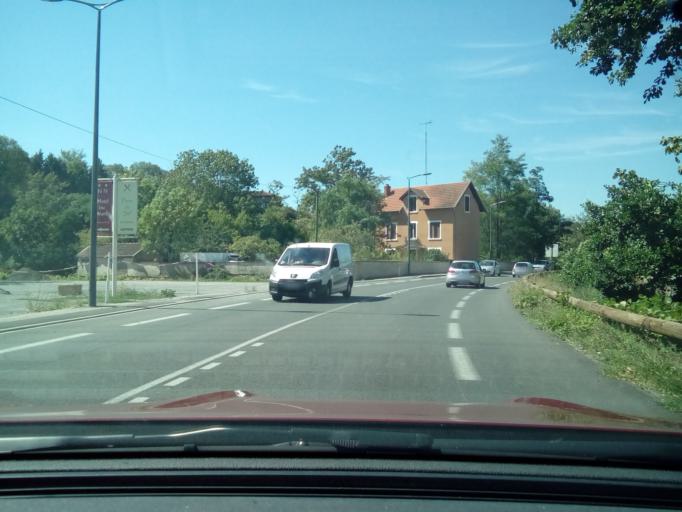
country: FR
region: Rhone-Alpes
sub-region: Departement du Rhone
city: Lozanne
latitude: 45.8559
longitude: 4.6779
